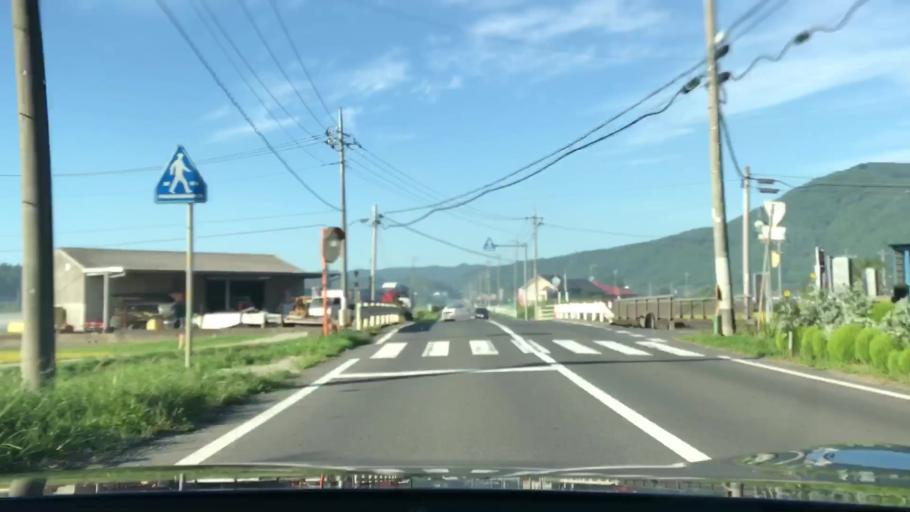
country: JP
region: Ibaraki
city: Makabe
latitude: 36.2586
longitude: 140.1723
